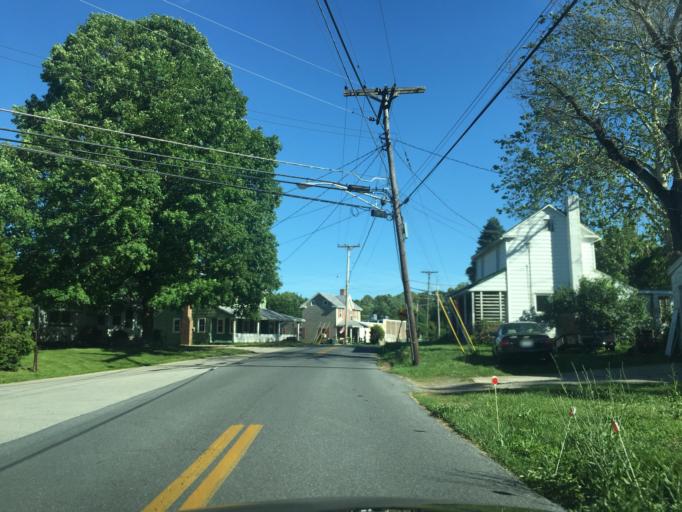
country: US
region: Maryland
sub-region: Baltimore County
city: Reisterstown
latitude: 39.5318
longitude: -76.8230
